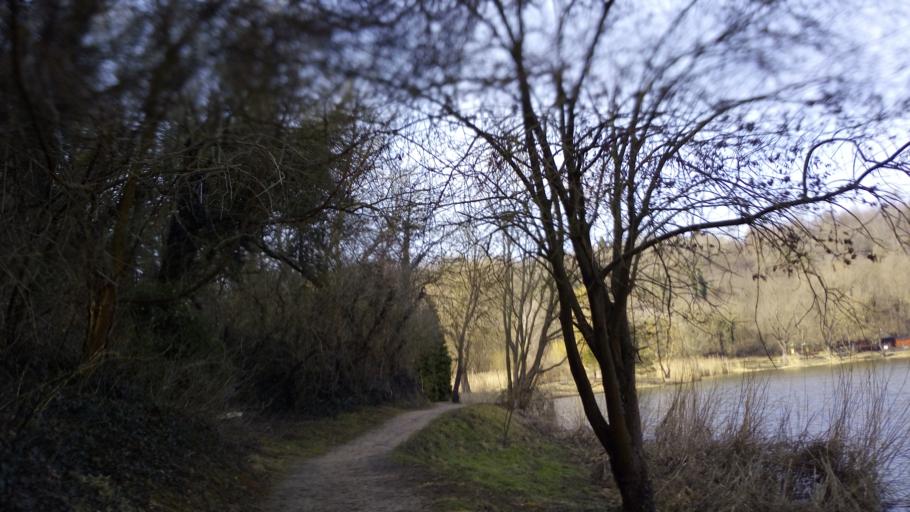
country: HU
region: Baranya
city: Pellerd
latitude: 46.0041
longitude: 18.2043
